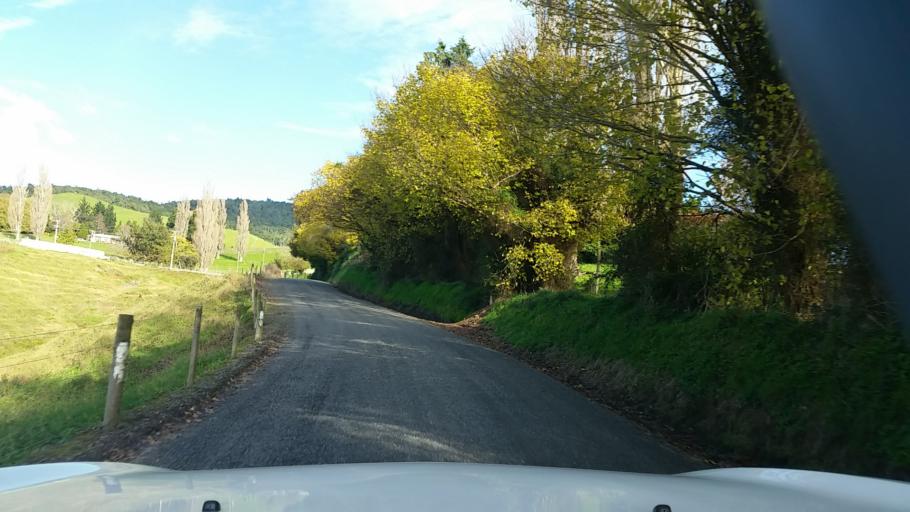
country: NZ
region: Waikato
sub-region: Matamata-Piako District
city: Matamata
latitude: -37.7952
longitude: 175.6339
